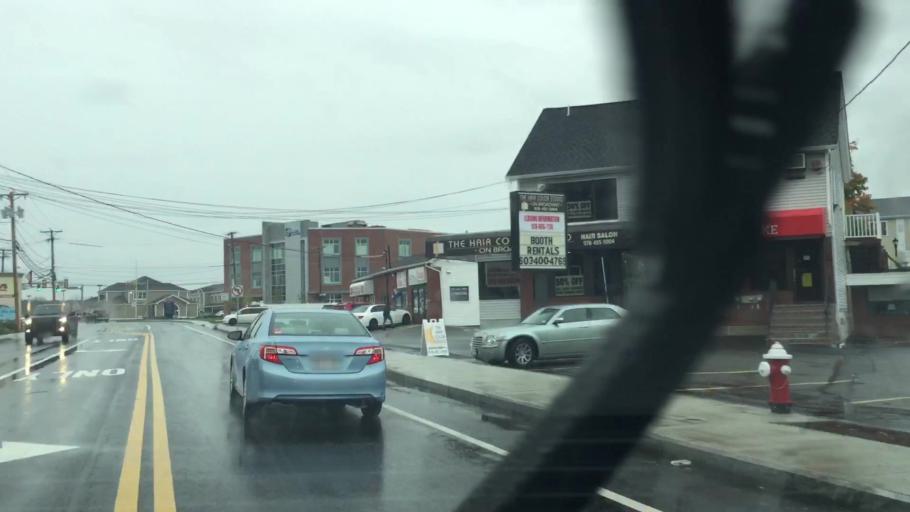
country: US
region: Massachusetts
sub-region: Middlesex County
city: Dracut
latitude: 42.6705
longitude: -71.2963
